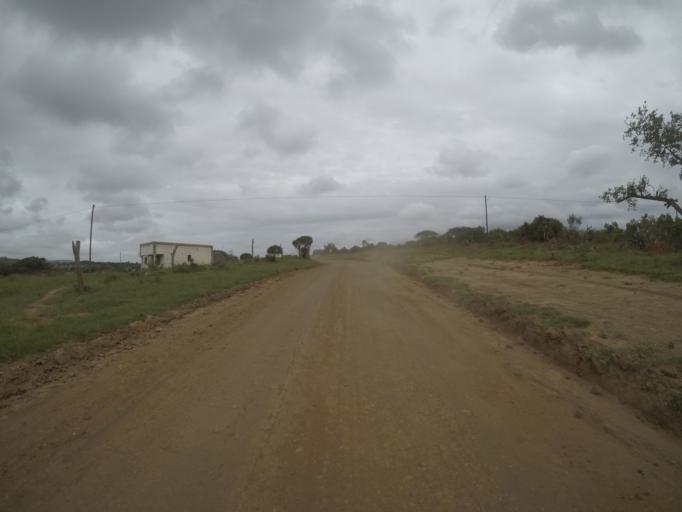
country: ZA
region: KwaZulu-Natal
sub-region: uThungulu District Municipality
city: Empangeni
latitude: -28.5946
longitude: 31.8403
